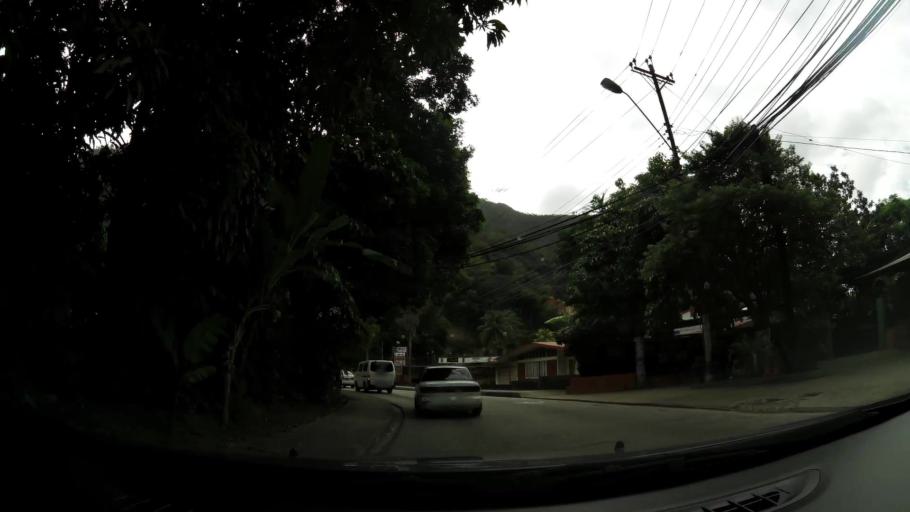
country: TT
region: Diego Martin
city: Petit Valley
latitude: 10.7051
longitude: -61.5119
